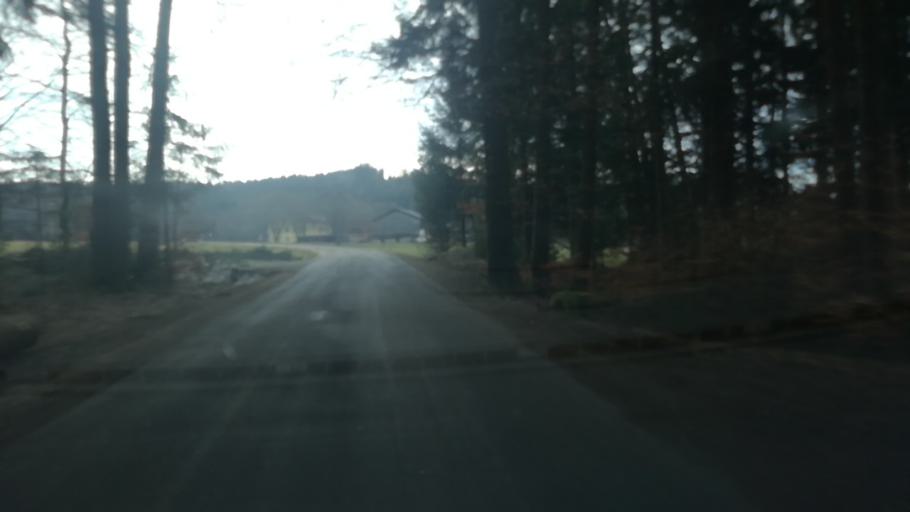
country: AT
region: Upper Austria
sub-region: Politischer Bezirk Vocklabruck
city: Redleiten
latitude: 48.0577
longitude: 13.5286
